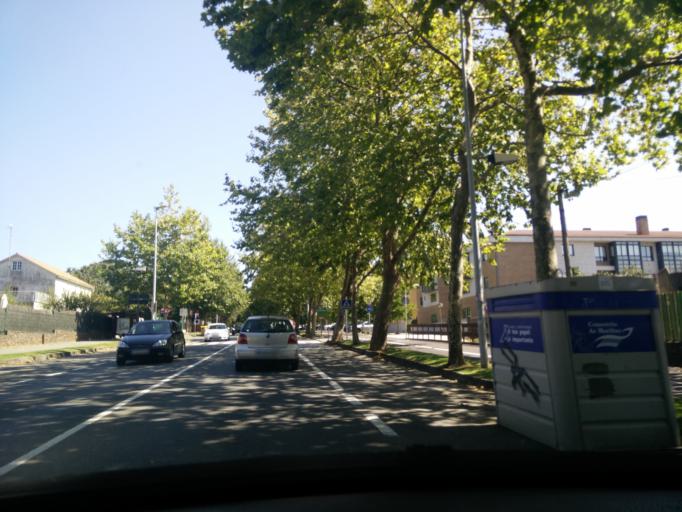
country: ES
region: Galicia
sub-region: Provincia da Coruna
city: Oleiros
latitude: 43.3404
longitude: -8.3515
